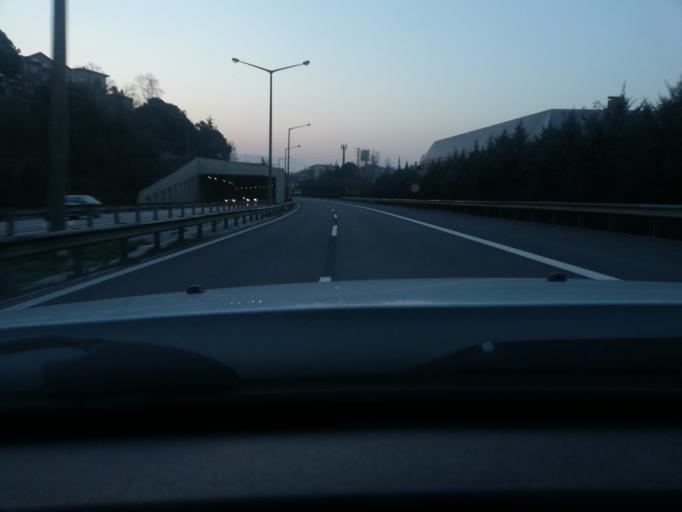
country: TR
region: Kocaeli
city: Derince
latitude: 40.7635
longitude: 29.8564
